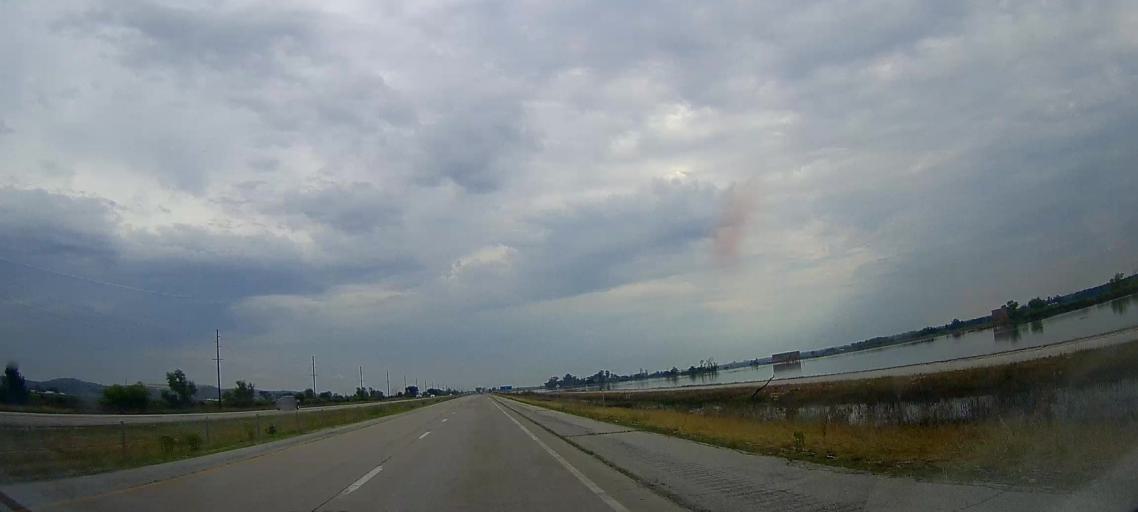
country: US
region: Iowa
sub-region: Pottawattamie County
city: Carter Lake
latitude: 41.3821
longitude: -95.8997
